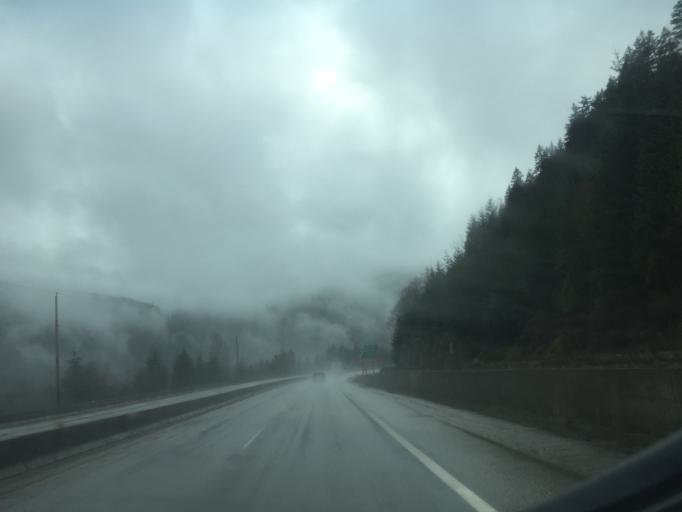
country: CA
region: British Columbia
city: Hope
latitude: 49.4983
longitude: -121.2038
